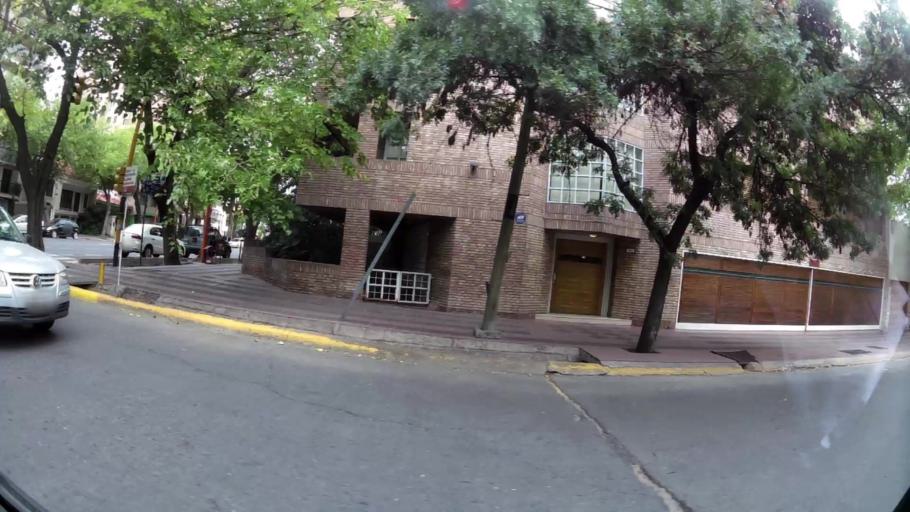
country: AR
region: Mendoza
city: Mendoza
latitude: -32.8877
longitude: -68.8538
